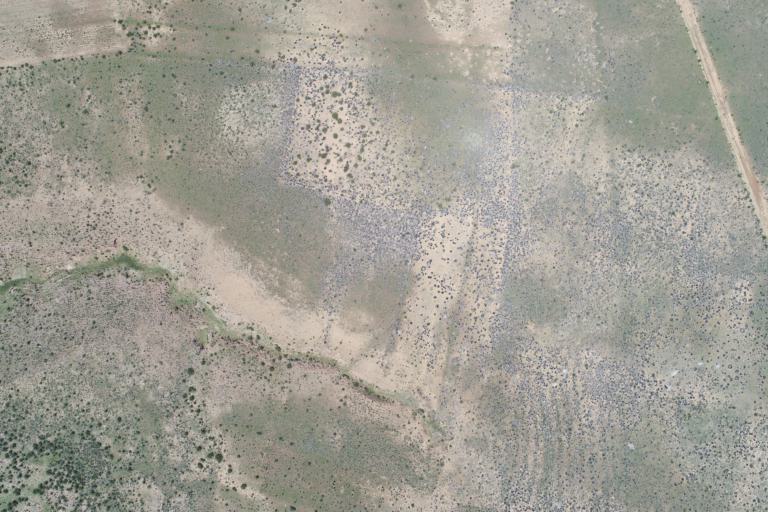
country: BO
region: La Paz
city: Curahuara de Carangas
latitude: -17.3114
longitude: -68.5114
